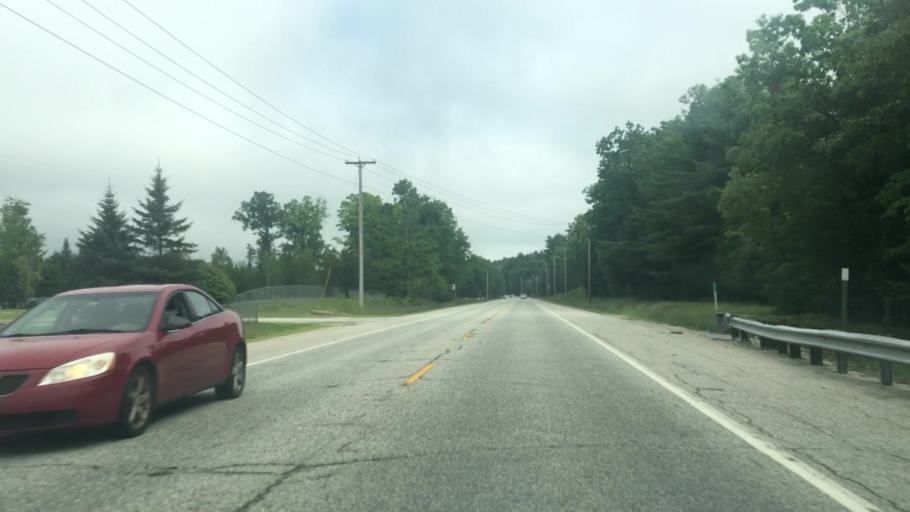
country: US
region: Maine
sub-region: Oxford County
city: Paris
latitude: 44.2460
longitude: -70.5132
